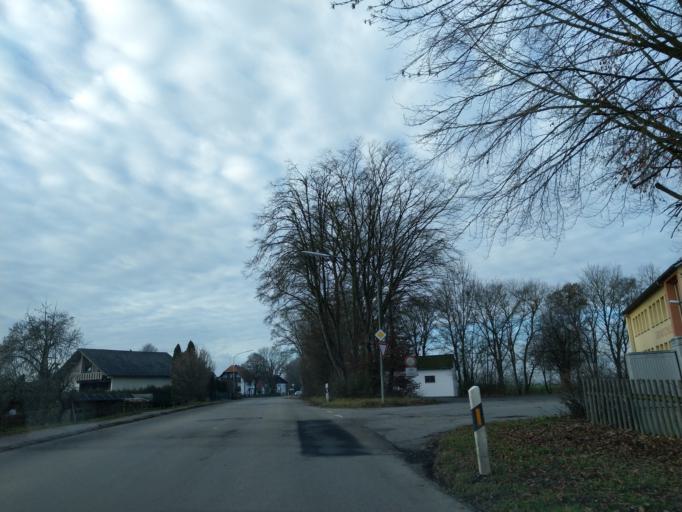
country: DE
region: Bavaria
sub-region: Lower Bavaria
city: Buchhofen
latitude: 48.6959
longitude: 12.9219
